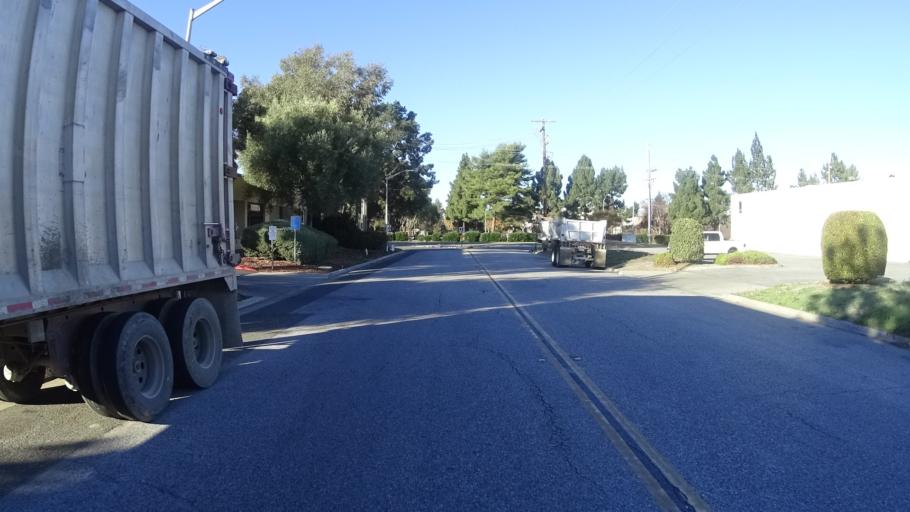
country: US
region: California
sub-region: Santa Clara County
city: Sunnyvale
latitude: 37.3768
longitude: -121.9940
